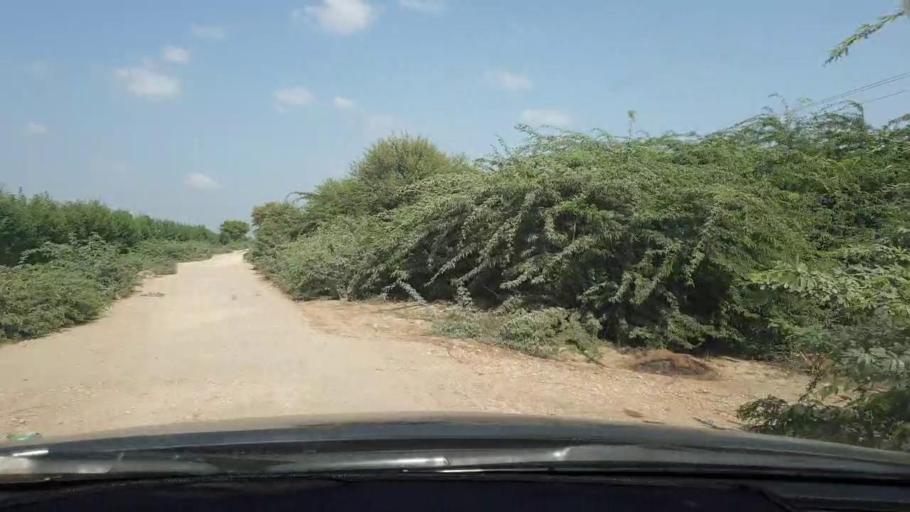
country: PK
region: Sindh
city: Naukot
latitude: 24.8801
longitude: 69.2662
